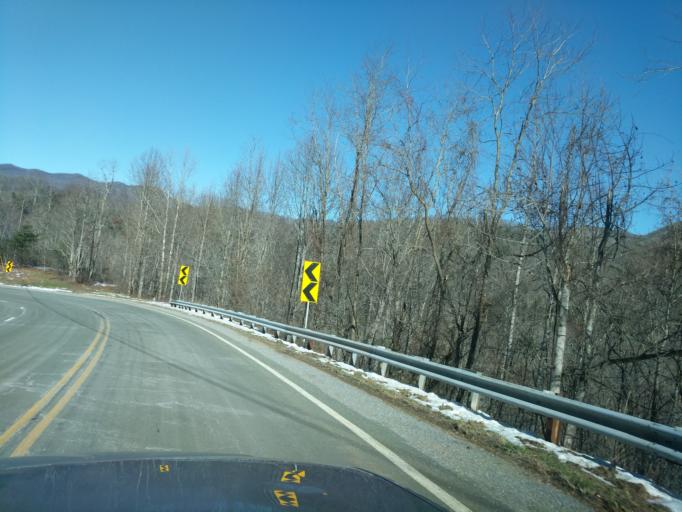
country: US
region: Georgia
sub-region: Towns County
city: Hiawassee
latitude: 34.9221
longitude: -83.6241
